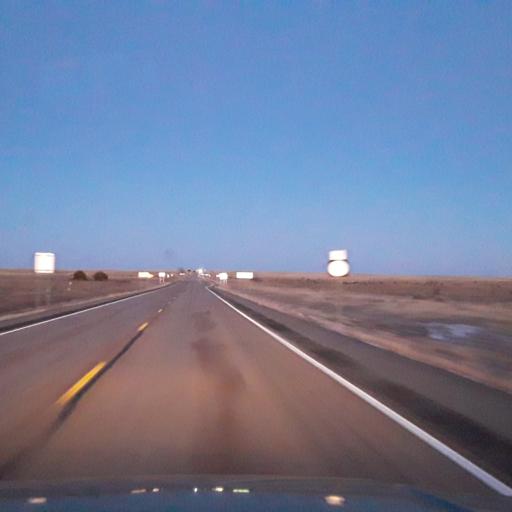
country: US
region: New Mexico
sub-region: Guadalupe County
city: Santa Rosa
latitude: 34.7827
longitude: -104.9383
